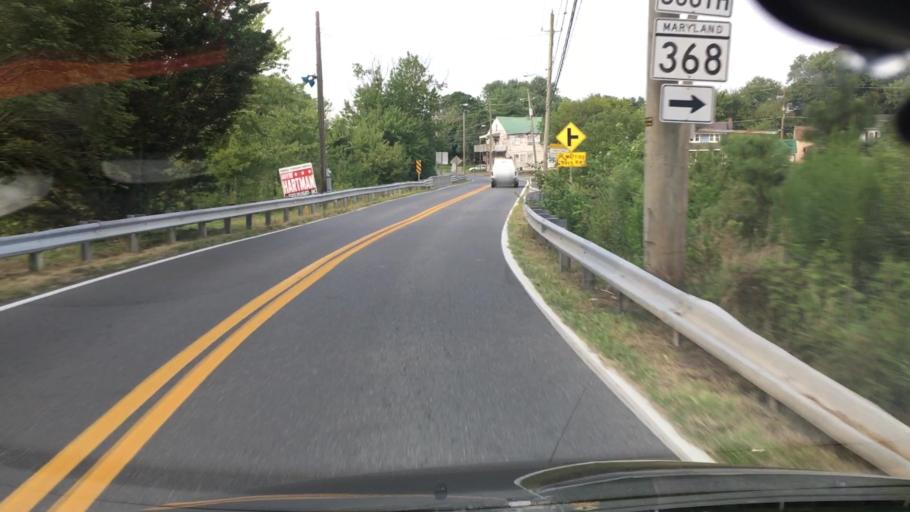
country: US
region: Delaware
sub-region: Sussex County
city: Selbyville
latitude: 38.4418
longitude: -75.1948
